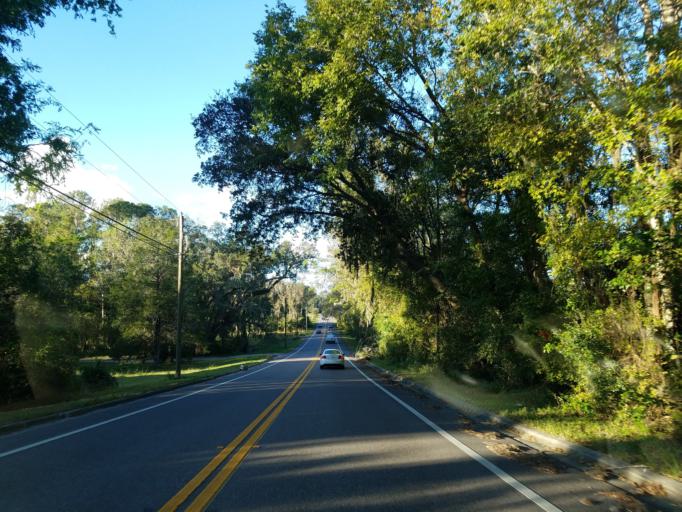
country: US
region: Florida
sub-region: Hernando County
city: Hill 'n Dale
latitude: 28.5000
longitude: -82.3030
